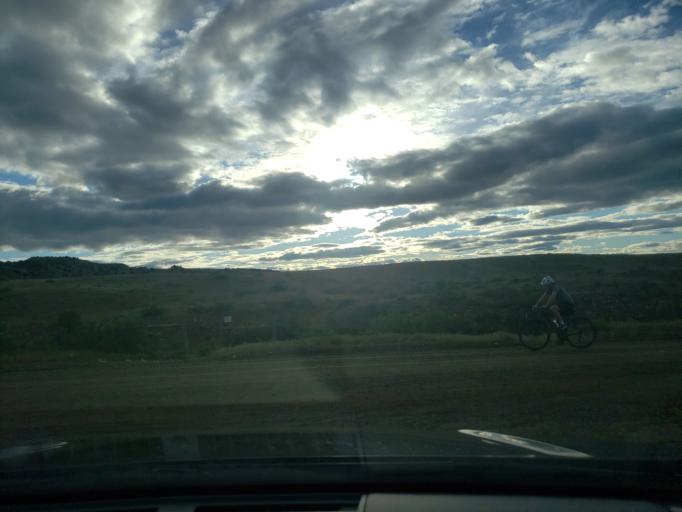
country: US
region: Colorado
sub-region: Mesa County
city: Fruita
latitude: 39.1441
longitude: -108.7584
